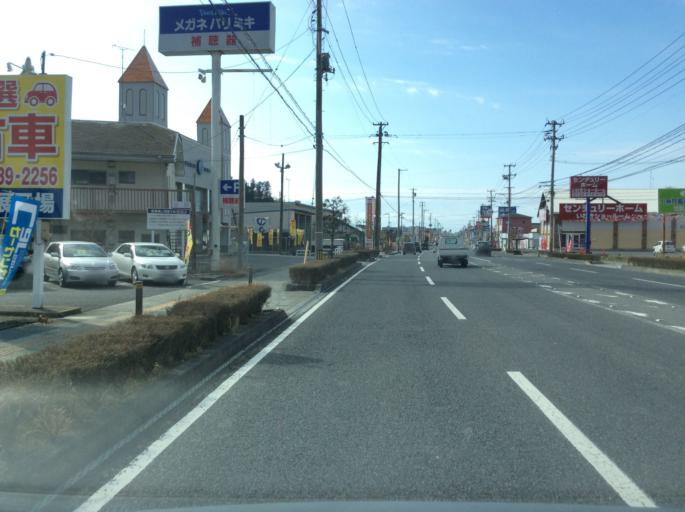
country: JP
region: Fukushima
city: Iwaki
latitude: 36.9695
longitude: 140.9052
